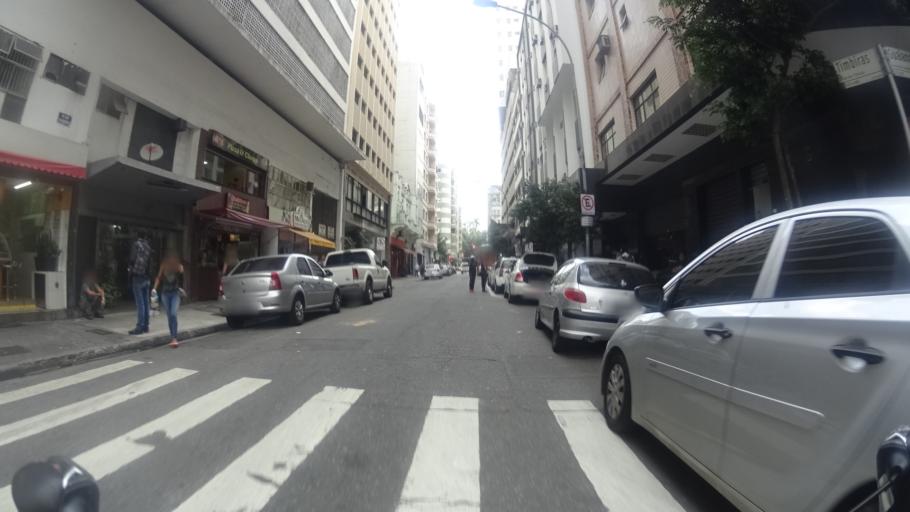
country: BR
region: Sao Paulo
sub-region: Sao Paulo
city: Sao Paulo
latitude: -23.5412
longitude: -46.6402
